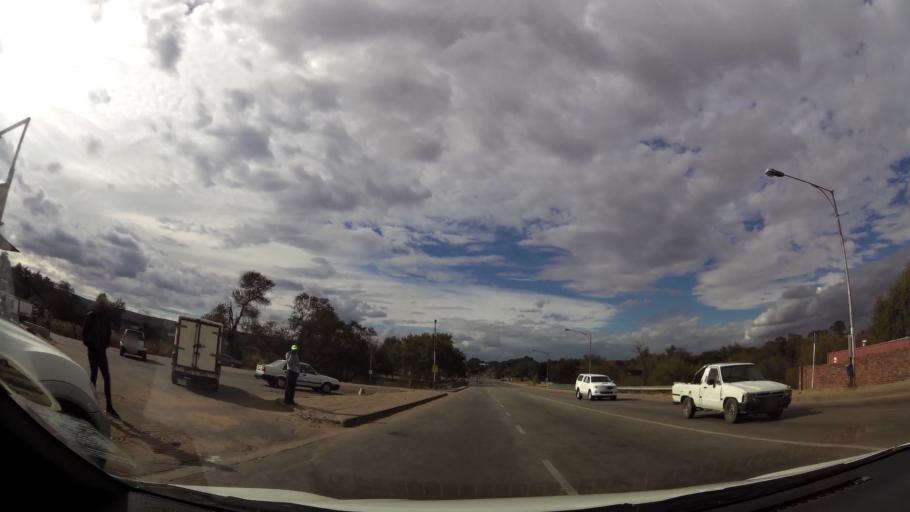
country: ZA
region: Limpopo
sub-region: Waterberg District Municipality
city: Modimolle
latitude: -24.6997
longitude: 28.4062
